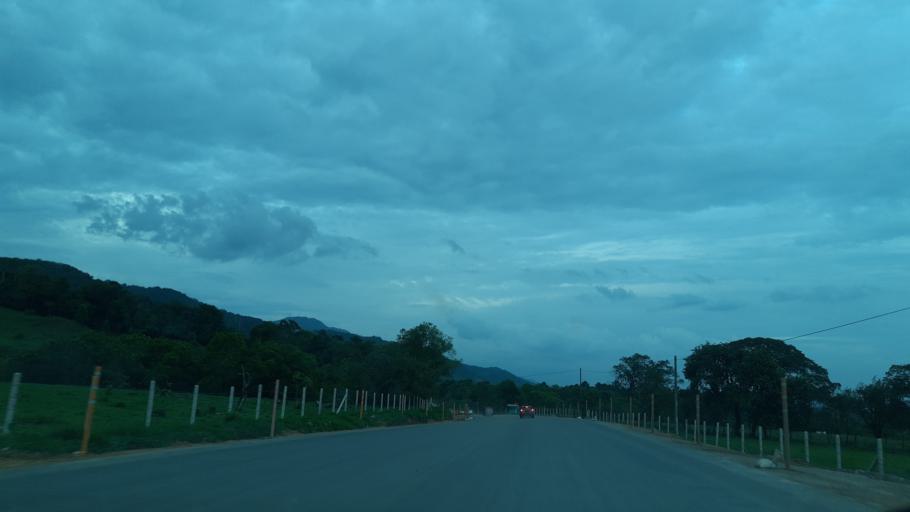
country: CO
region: Casanare
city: Sabanalarga
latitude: 4.7664
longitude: -73.0059
